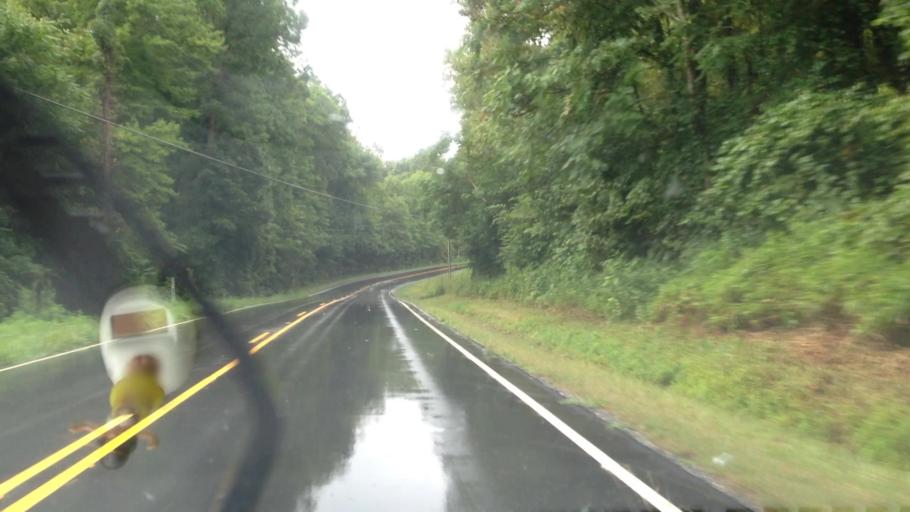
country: US
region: North Carolina
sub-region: Stokes County
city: Danbury
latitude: 36.4418
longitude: -80.1039
